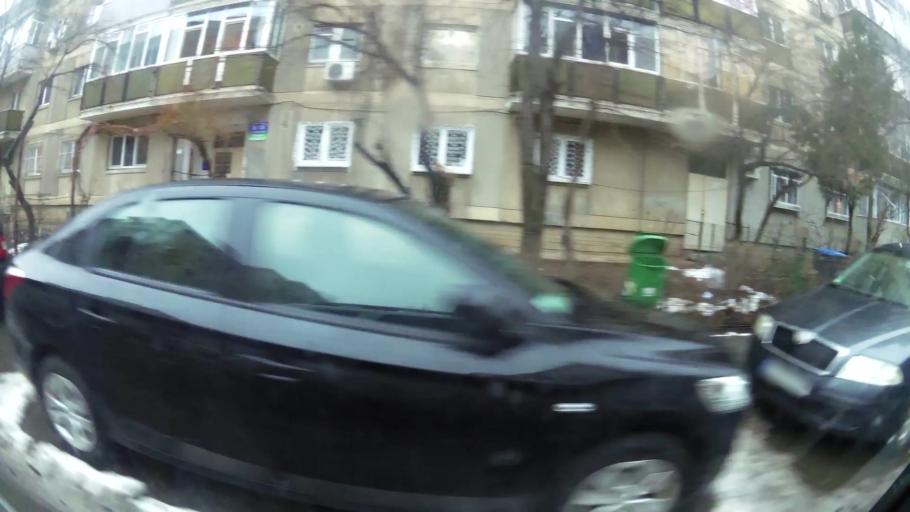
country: RO
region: Ilfov
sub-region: Comuna Chiajna
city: Rosu
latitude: 44.4309
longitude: 26.0170
